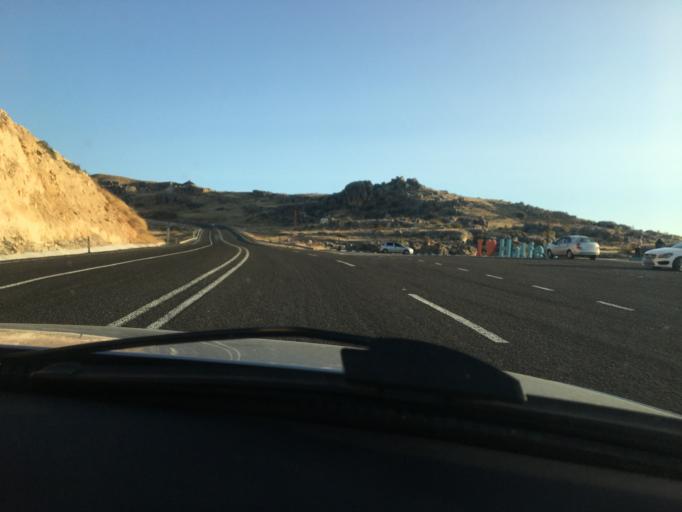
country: TR
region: Sanliurfa
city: Halfeti
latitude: 37.2416
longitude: 37.8753
